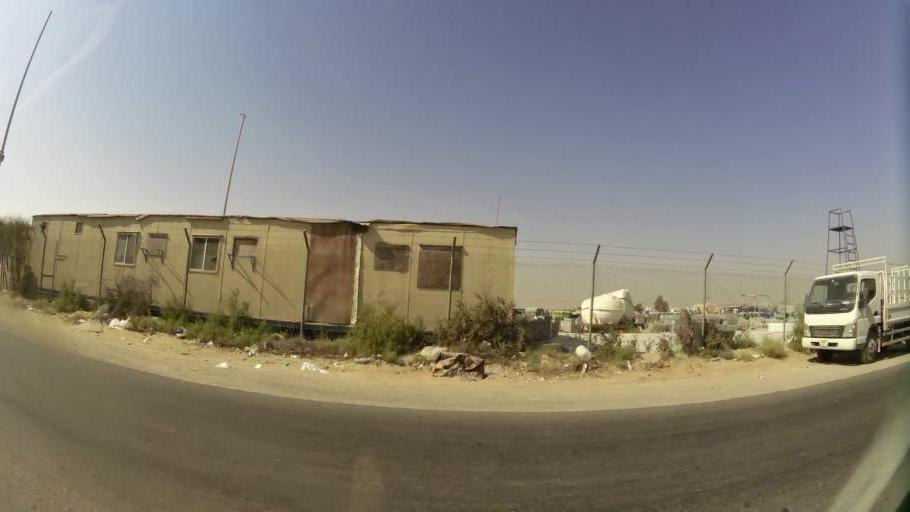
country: AE
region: Ajman
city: Ajman
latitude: 25.4306
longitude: 55.5438
